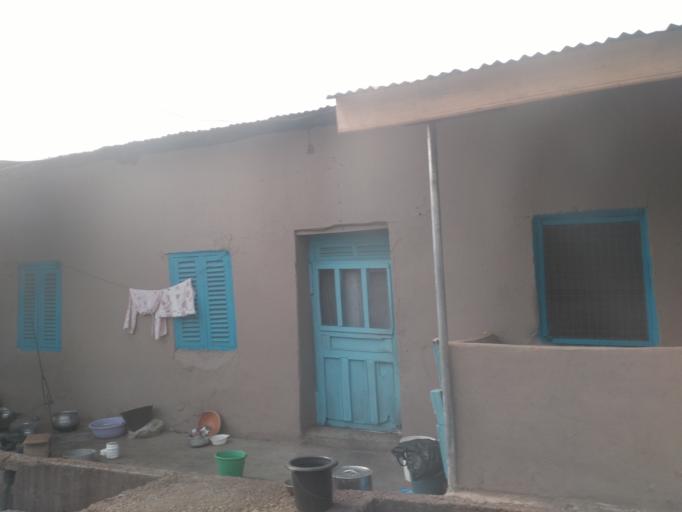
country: GH
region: Ashanti
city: Kumasi
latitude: 6.7031
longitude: -1.6191
